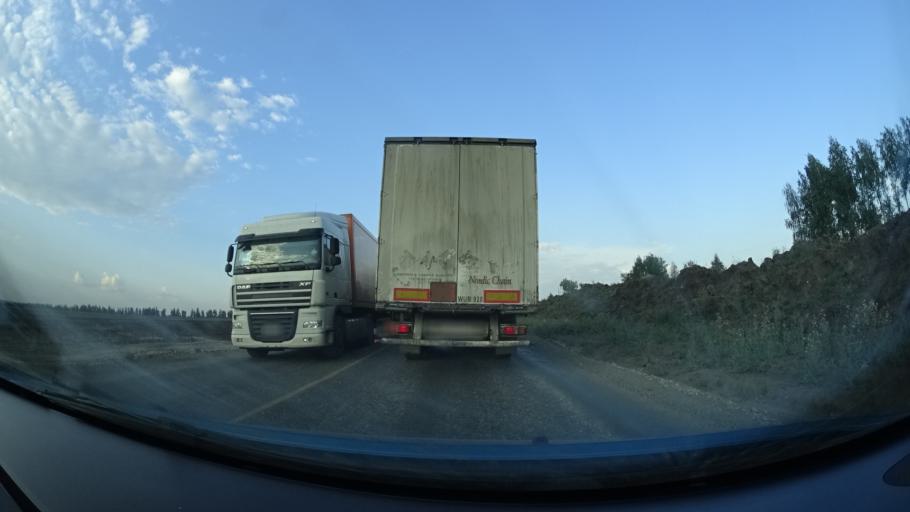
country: RU
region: Samara
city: Kamyshla
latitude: 54.0430
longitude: 51.9906
